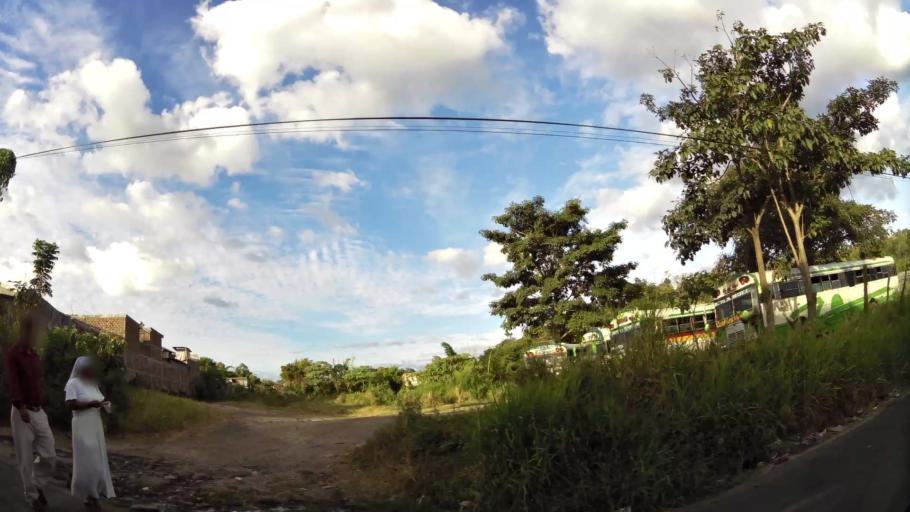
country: SV
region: Cuscatlan
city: Cojutepeque
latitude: 13.7180
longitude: -88.9286
